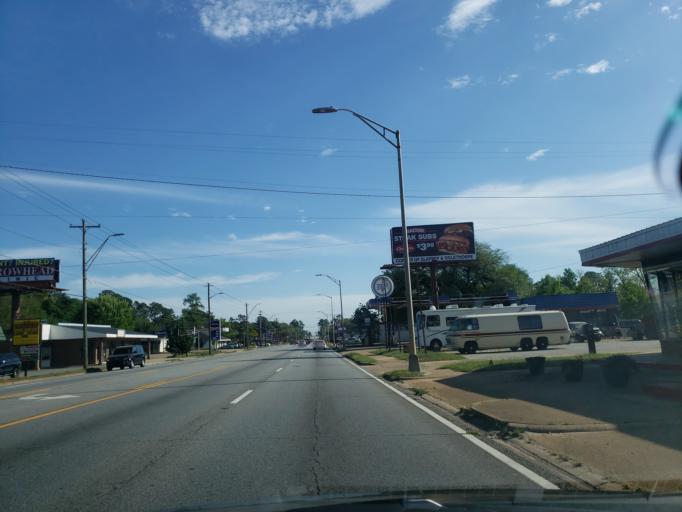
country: US
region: Georgia
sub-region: Dougherty County
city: Albany
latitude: 31.5940
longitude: -84.1761
